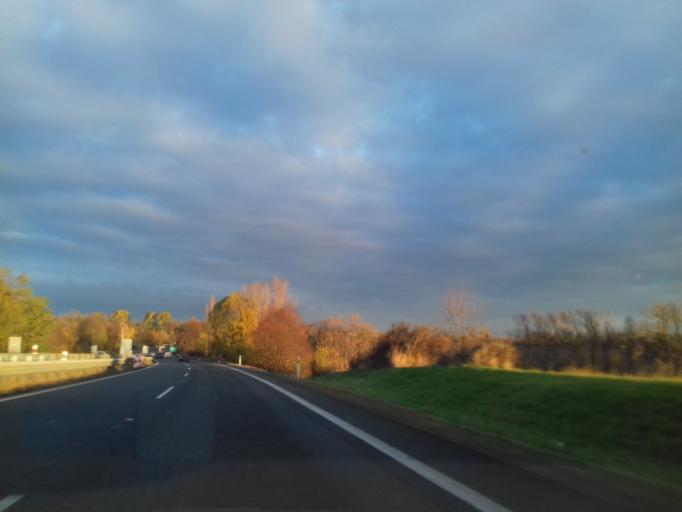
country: CZ
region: Olomoucky
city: Urcice
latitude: 49.4306
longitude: 17.1115
